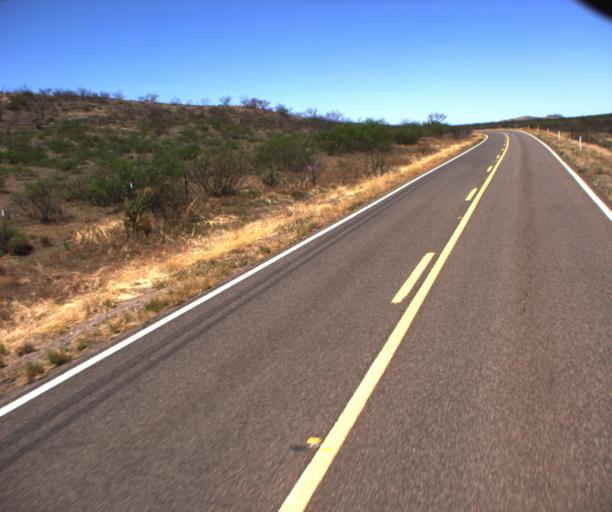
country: US
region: Arizona
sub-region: Cochise County
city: Douglas
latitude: 31.4895
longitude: -109.4217
